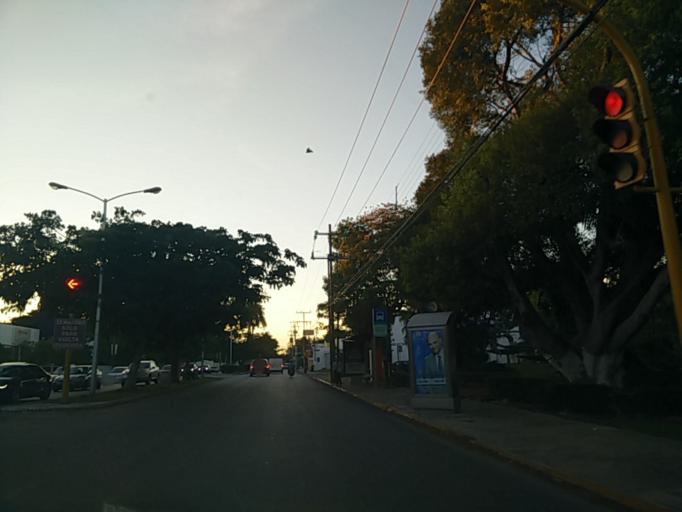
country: MX
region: Yucatan
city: Merida
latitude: 20.9979
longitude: -89.6099
